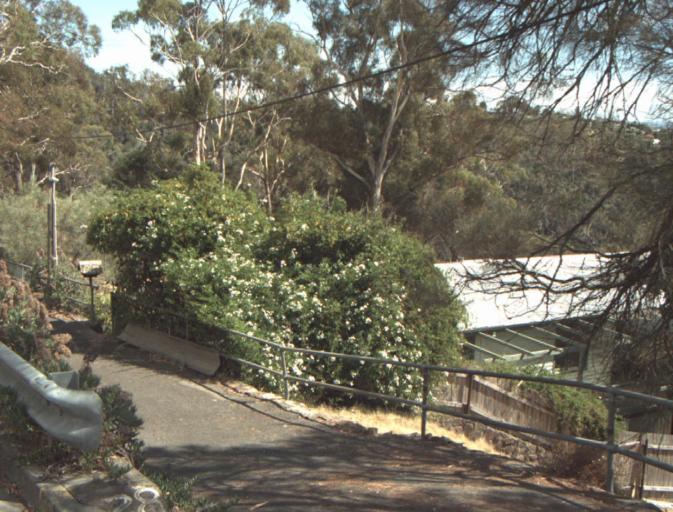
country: AU
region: Tasmania
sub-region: Launceston
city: West Launceston
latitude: -41.4487
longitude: 147.1221
